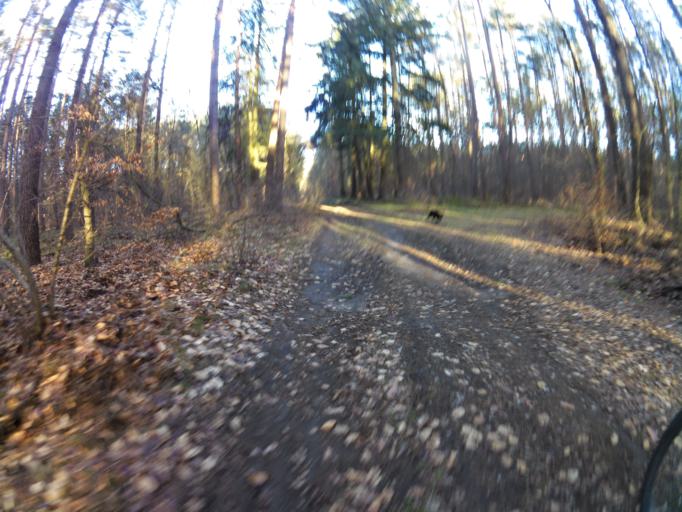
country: PL
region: West Pomeranian Voivodeship
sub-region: Powiat mysliborski
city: Debno
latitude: 52.8239
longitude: 14.7519
